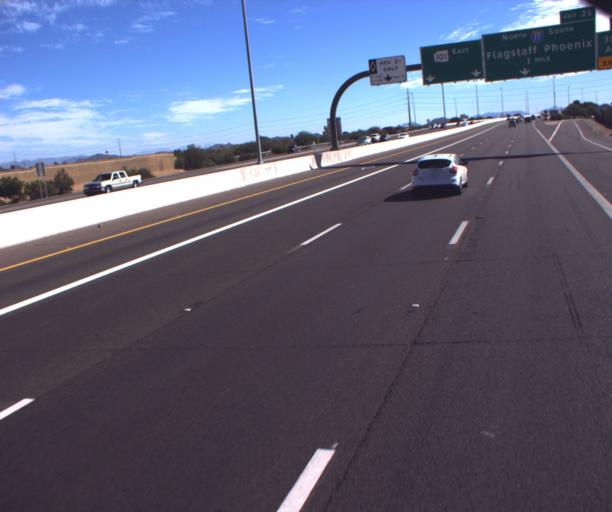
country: US
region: Arizona
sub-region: Maricopa County
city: Peoria
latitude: 33.6695
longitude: -112.1407
